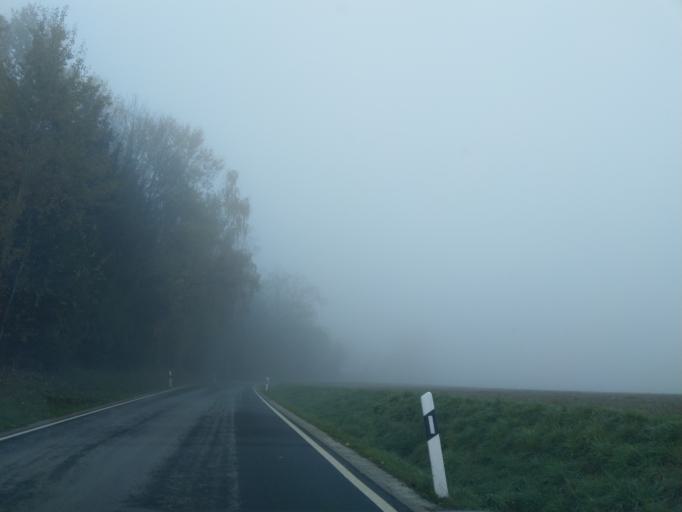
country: DE
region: Bavaria
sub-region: Lower Bavaria
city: Hengersberg
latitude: 48.7658
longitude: 13.0917
